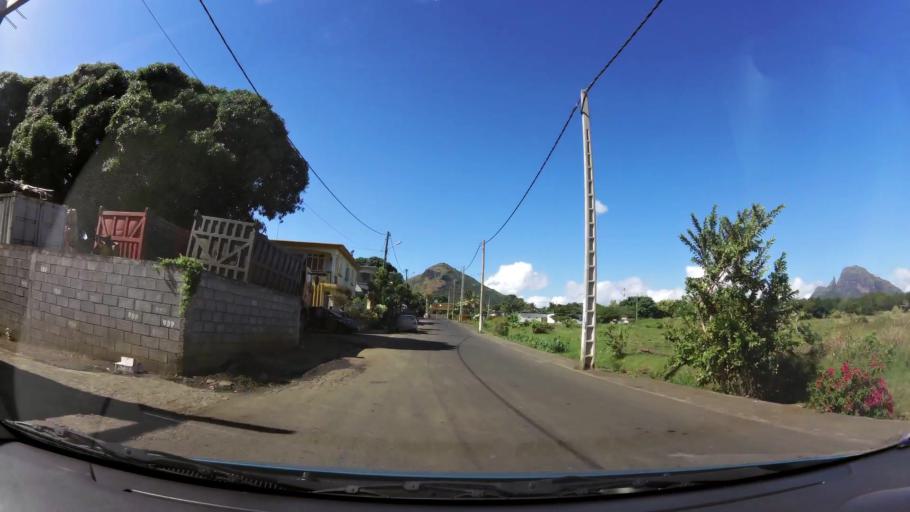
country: MU
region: Black River
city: Cascavelle
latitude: -20.2616
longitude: 57.4091
